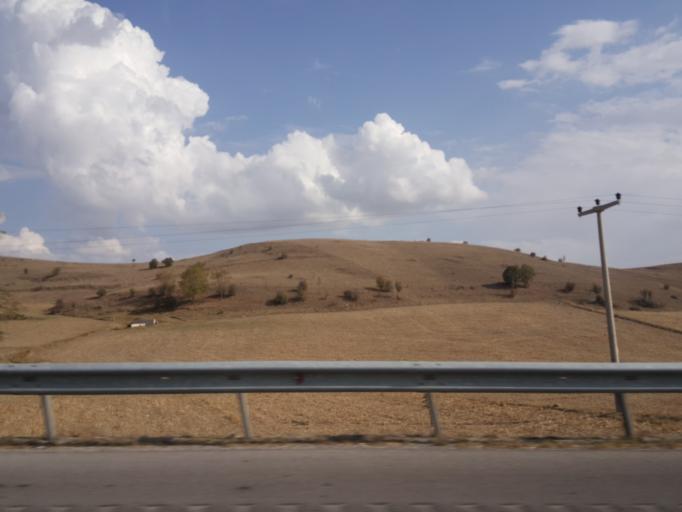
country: TR
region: Corum
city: Alaca
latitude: 40.2894
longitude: 34.6512
